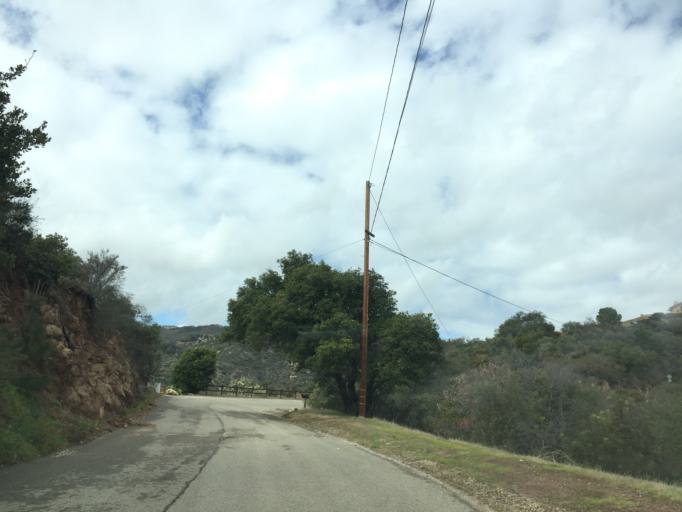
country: US
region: California
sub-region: Santa Barbara County
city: Goleta
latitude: 34.4817
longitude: -119.7975
